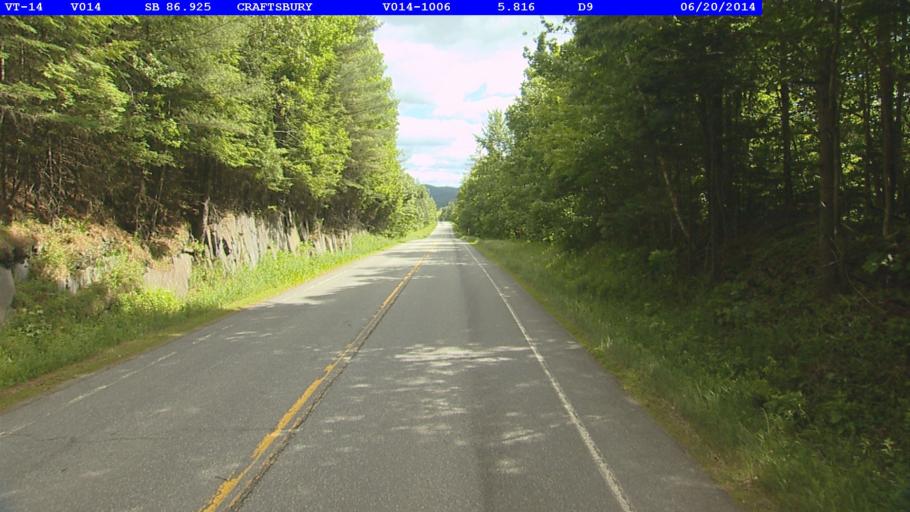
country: US
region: Vermont
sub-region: Caledonia County
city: Hardwick
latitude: 44.6743
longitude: -72.4048
